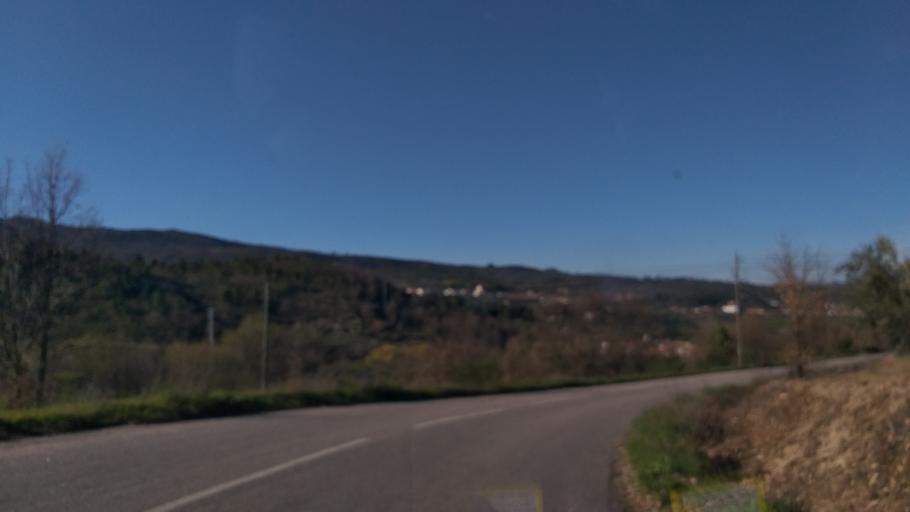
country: PT
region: Guarda
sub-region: Celorico da Beira
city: Celorico da Beira
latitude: 40.5895
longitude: -7.3622
